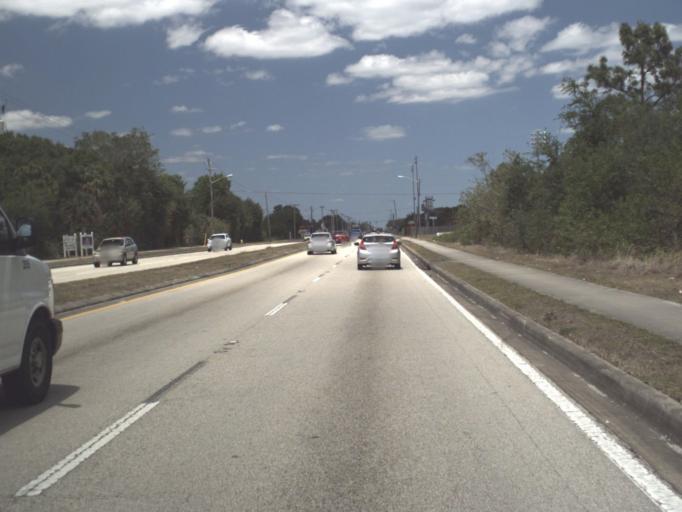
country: US
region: Florida
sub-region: Brevard County
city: Palm Bay
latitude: 28.0449
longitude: -80.6215
